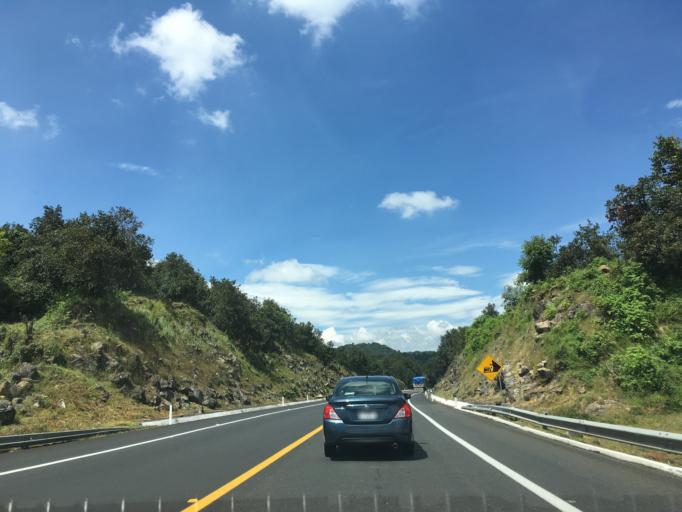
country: MX
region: Michoacan
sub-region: Patzcuaro
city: Colonia Vista Bella (Lomas del Peaje)
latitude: 19.4933
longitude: -101.6181
